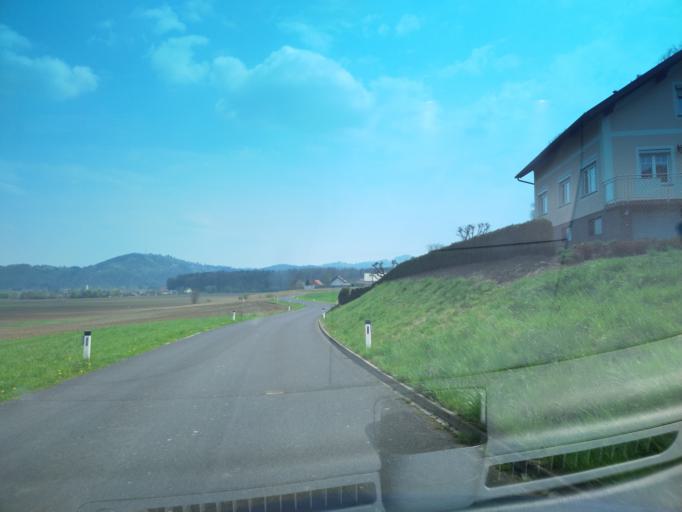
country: AT
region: Styria
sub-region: Politischer Bezirk Leibnitz
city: Kitzeck im Sausal
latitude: 46.7557
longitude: 15.4147
